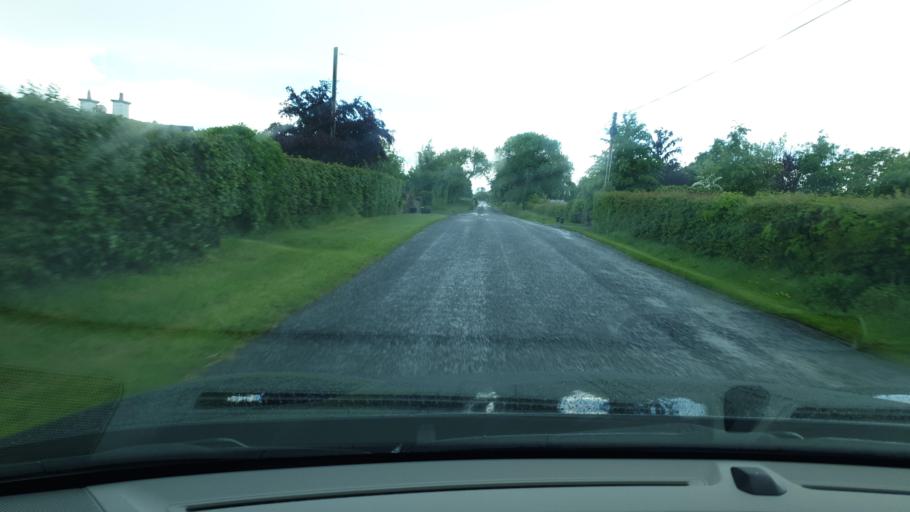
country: IE
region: Leinster
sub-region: Laois
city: Mountmellick
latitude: 53.1298
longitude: -7.3747
